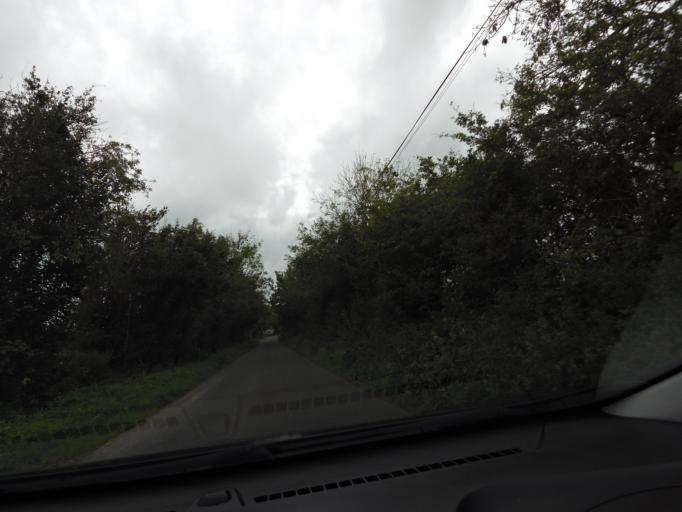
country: IE
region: Connaught
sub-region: County Galway
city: Athenry
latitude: 53.2755
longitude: -8.6827
